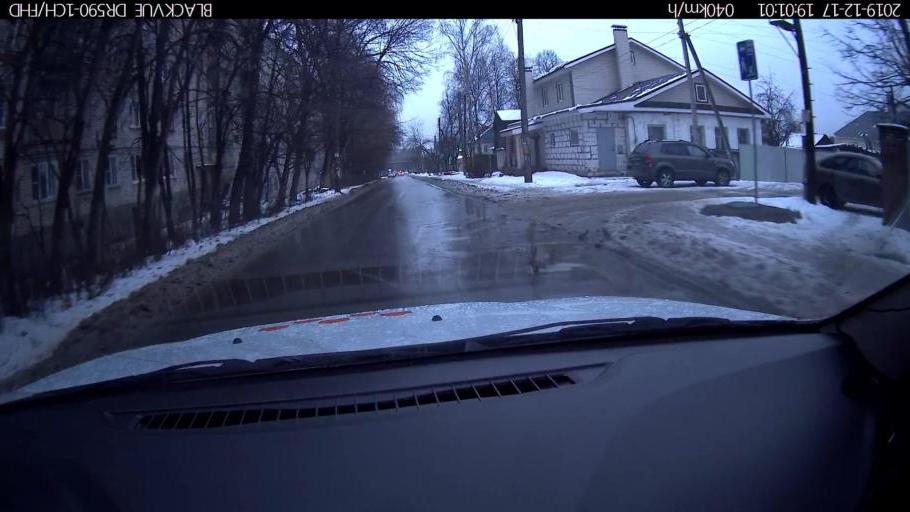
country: RU
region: Nizjnij Novgorod
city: Nizhniy Novgorod
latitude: 56.2925
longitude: 44.0285
